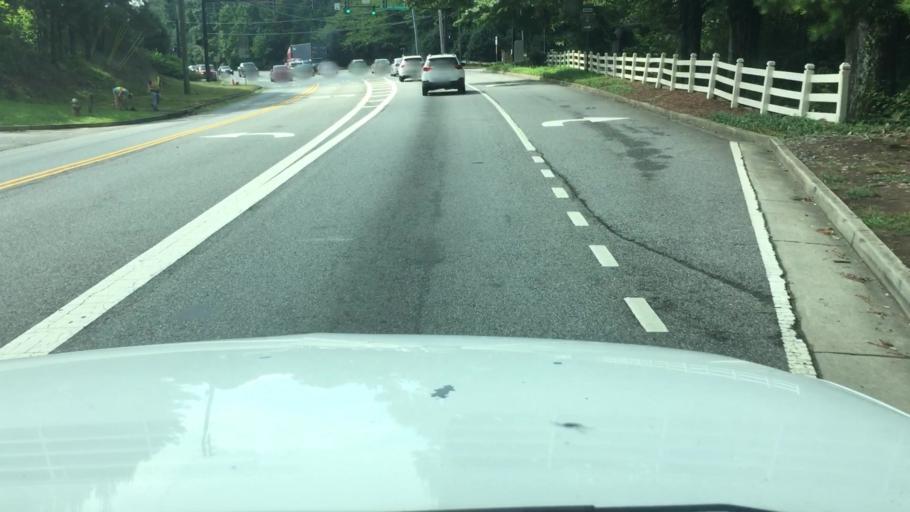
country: US
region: Georgia
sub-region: Fulton County
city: Johns Creek
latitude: 34.0949
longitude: -84.2103
